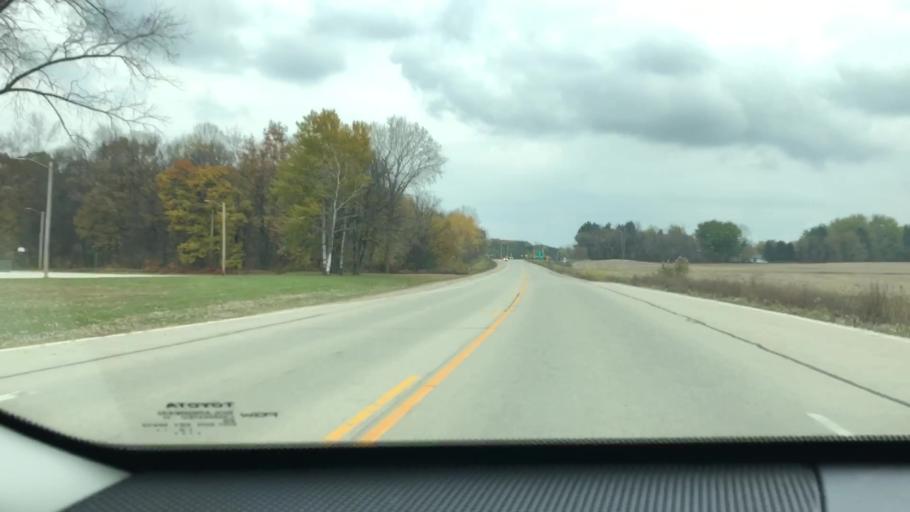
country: US
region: Wisconsin
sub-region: Brown County
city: Oneida
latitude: 44.4986
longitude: -88.1563
